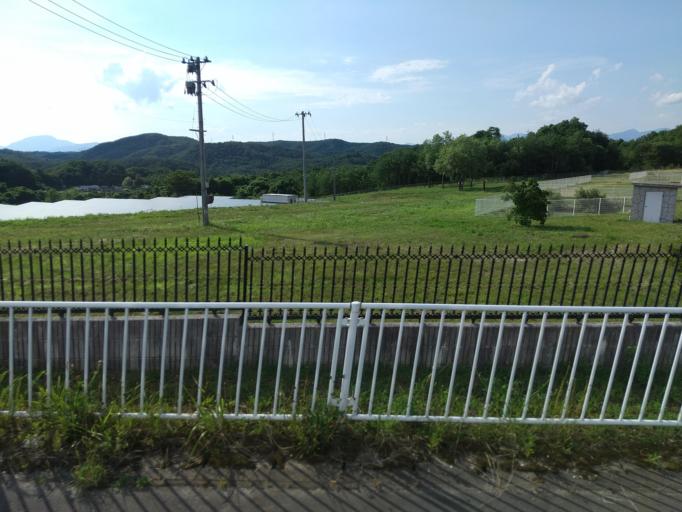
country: JP
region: Miyagi
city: Sendai
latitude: 38.2493
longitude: 140.7414
